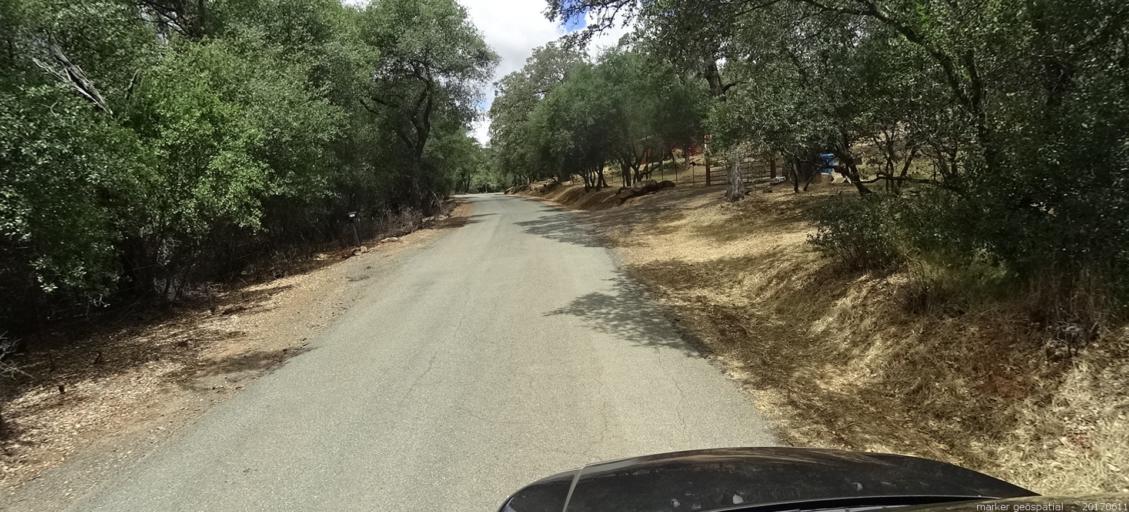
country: US
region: California
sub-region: Butte County
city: Oroville
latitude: 39.5960
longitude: -121.5313
